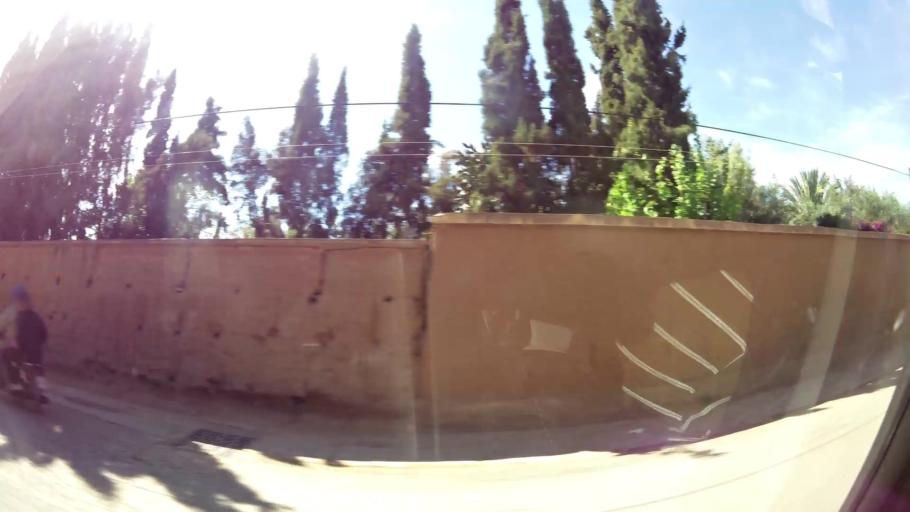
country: MA
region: Marrakech-Tensift-Al Haouz
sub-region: Marrakech
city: Marrakesh
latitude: 31.6273
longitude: -7.9606
